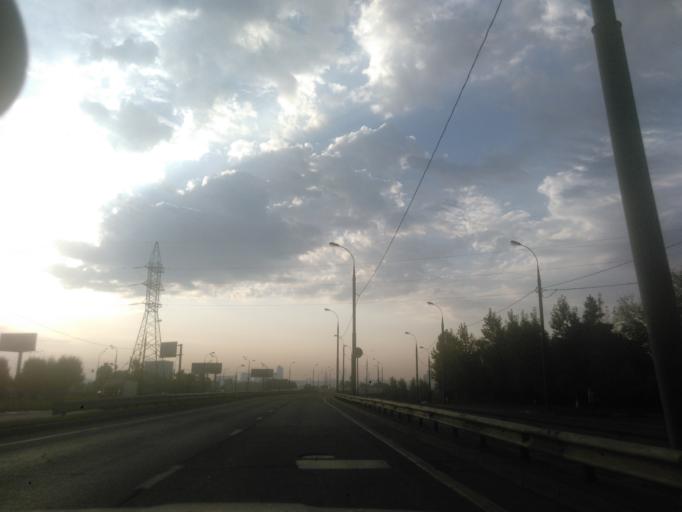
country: RU
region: Moscow
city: Strogino
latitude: 55.8352
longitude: 37.3855
